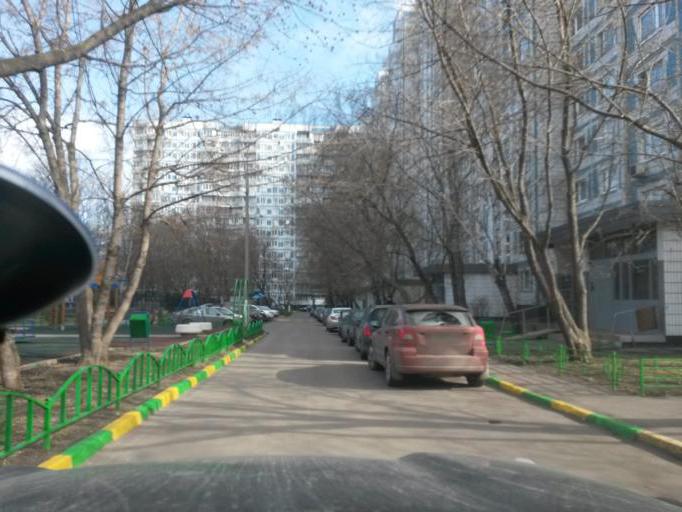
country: RU
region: Moscow
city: Mar'ino
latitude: 55.6447
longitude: 37.7263
